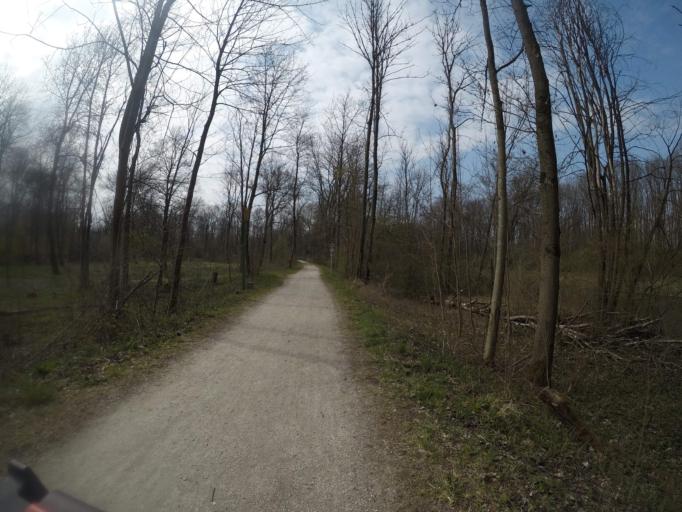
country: DE
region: Baden-Wuerttemberg
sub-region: Tuebingen Region
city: Ulm
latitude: 48.3795
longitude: 9.9721
